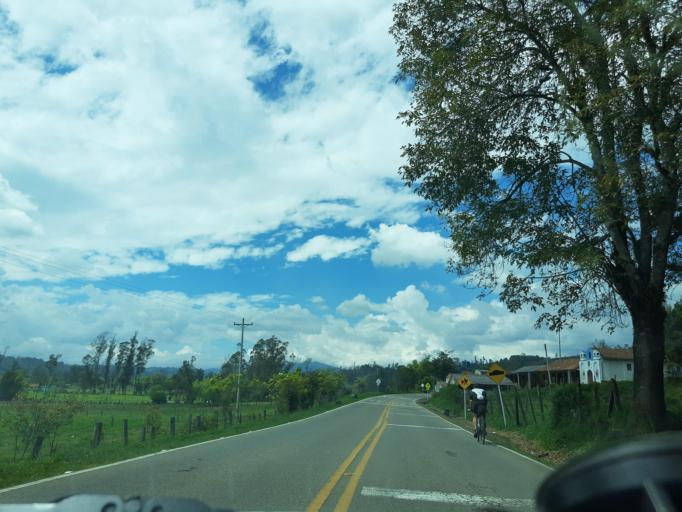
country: CO
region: Boyaca
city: Chiquinquira
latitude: 5.6044
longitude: -73.7222
